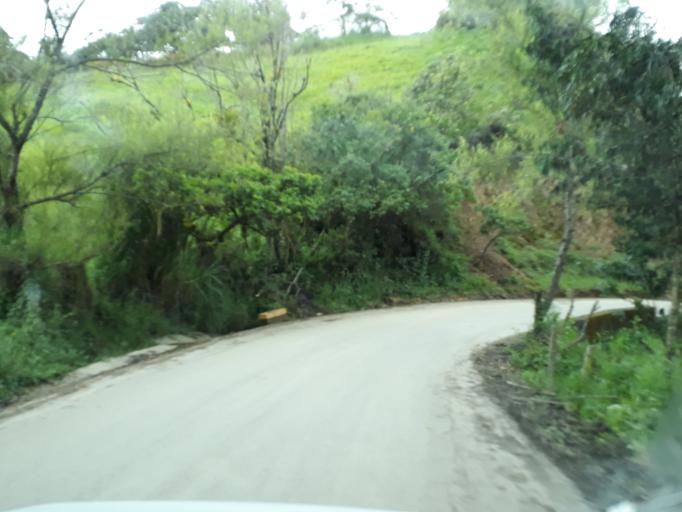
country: CO
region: Cundinamarca
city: Junin
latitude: 4.8176
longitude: -73.6665
